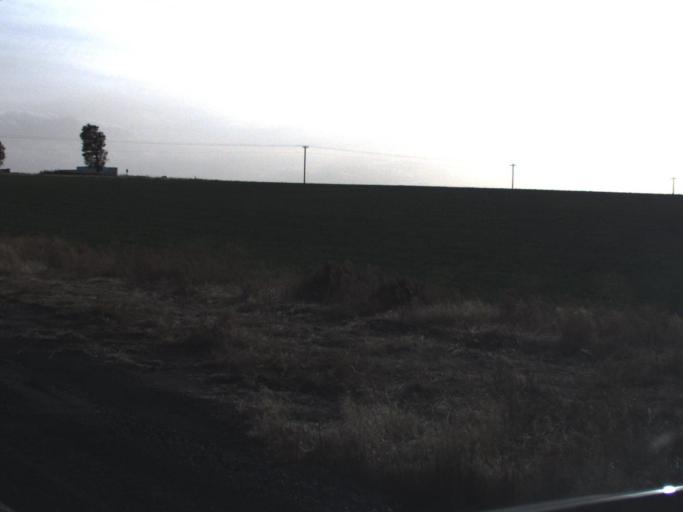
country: US
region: Washington
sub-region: Adams County
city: Ritzville
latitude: 47.2626
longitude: -118.6913
